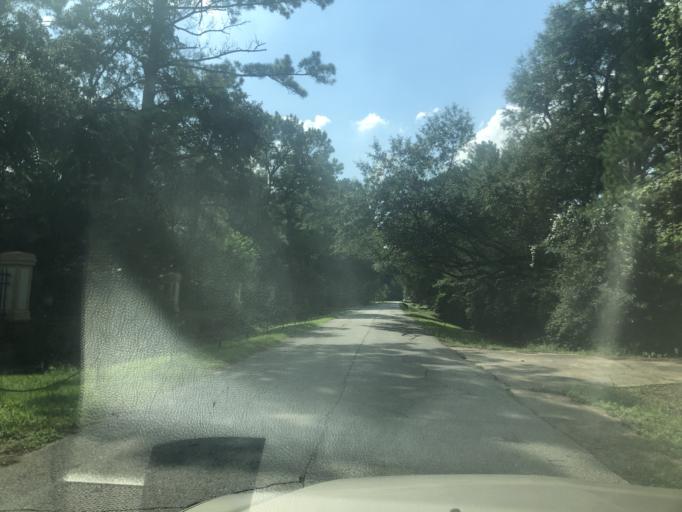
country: US
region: Texas
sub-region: Harris County
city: Bunker Hill Village
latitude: 29.7435
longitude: -95.5457
